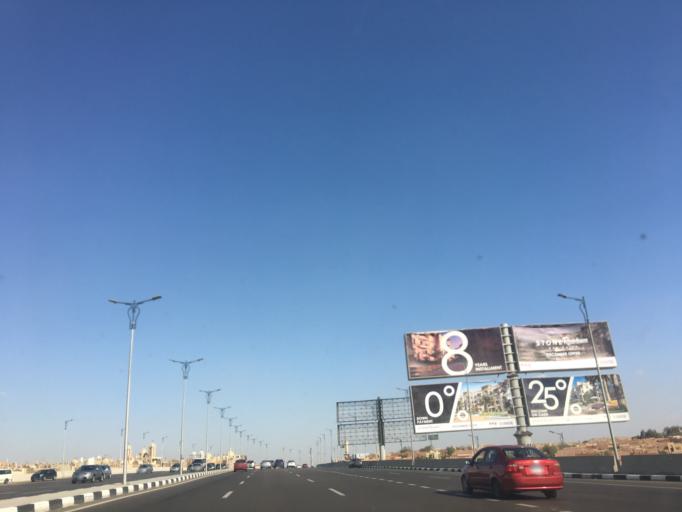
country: EG
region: Muhafazat al Qahirah
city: Cairo
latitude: 30.0204
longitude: 31.3454
